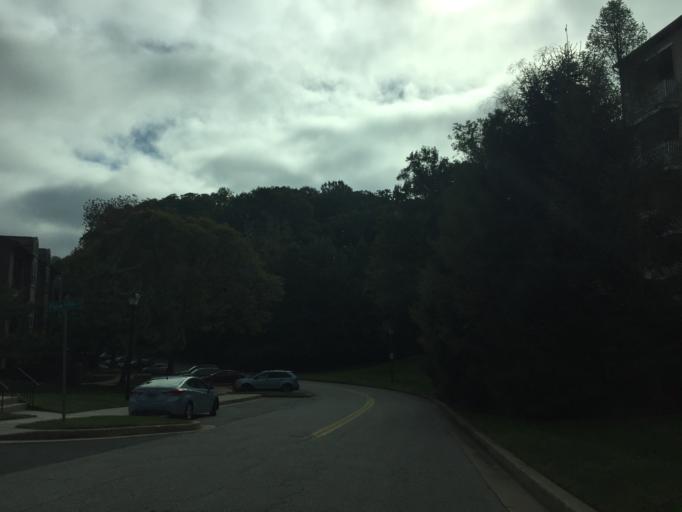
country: US
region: Maryland
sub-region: Baltimore County
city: Pikesville
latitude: 39.3816
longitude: -76.6704
